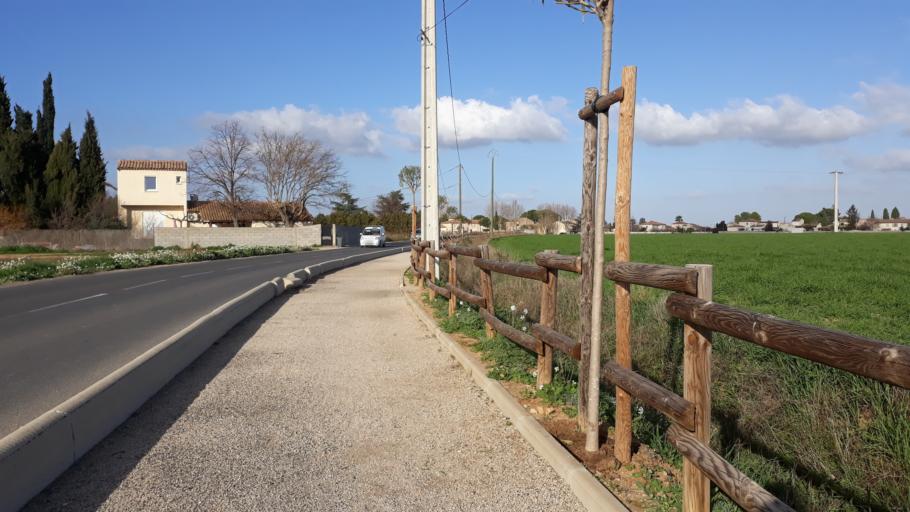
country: FR
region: Languedoc-Roussillon
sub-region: Departement du Gard
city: Aimargues
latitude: 43.6875
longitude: 4.1993
